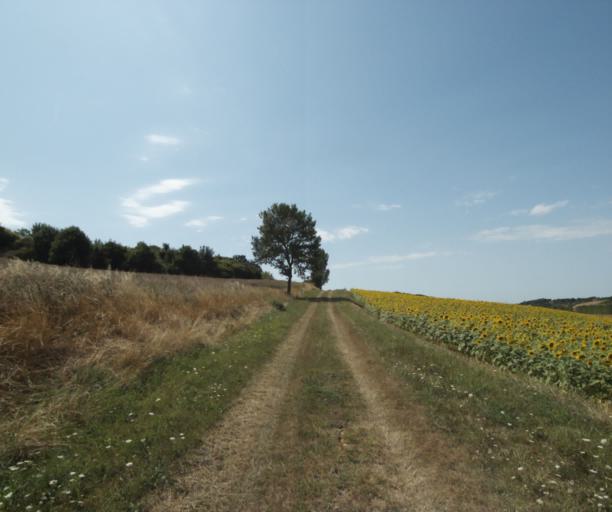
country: FR
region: Midi-Pyrenees
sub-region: Departement de la Haute-Garonne
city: Saint-Felix-Lauragais
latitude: 43.4567
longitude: 1.8729
